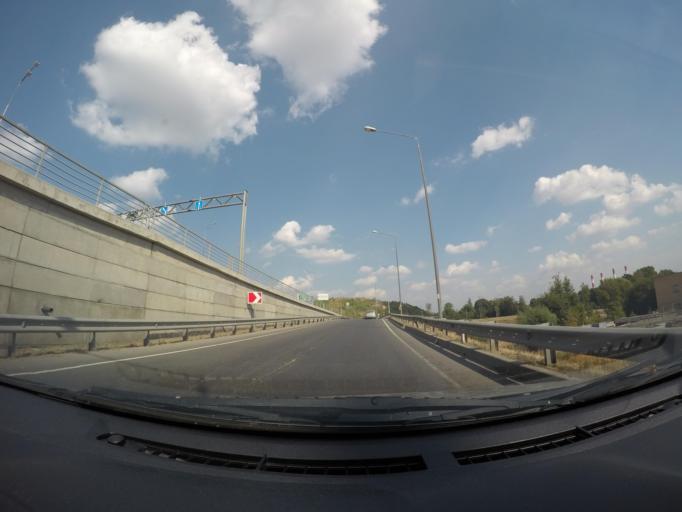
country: RU
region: Moskovskaya
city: Levoberezhnaya
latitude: 55.8973
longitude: 37.4877
